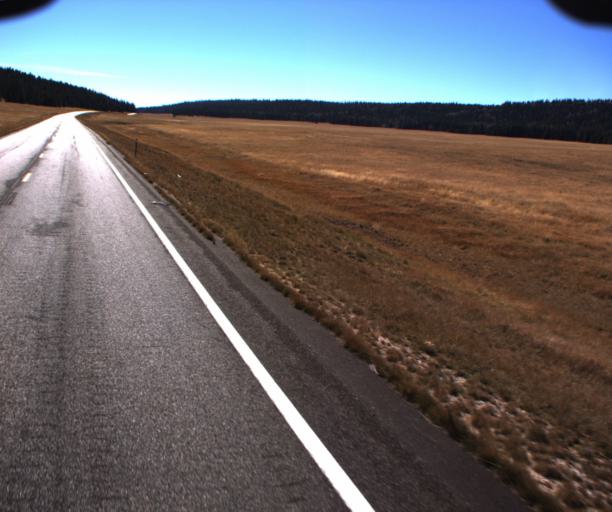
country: US
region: Arizona
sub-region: Coconino County
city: Grand Canyon
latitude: 36.3921
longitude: -112.1275
